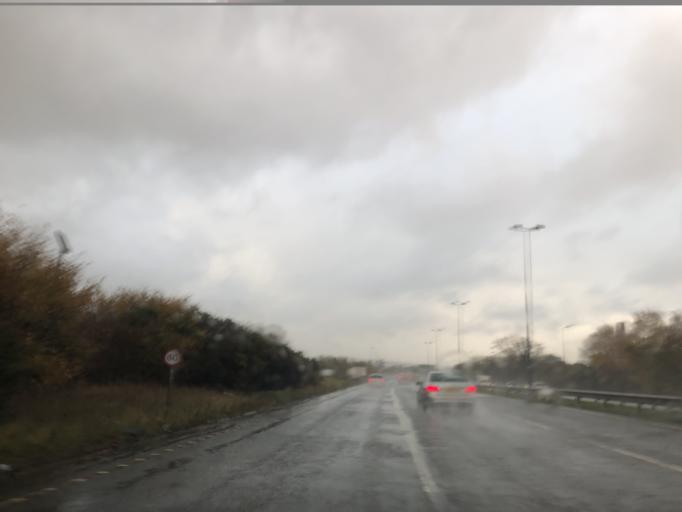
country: GB
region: England
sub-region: Solihull
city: Hampton in Arden
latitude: 52.4458
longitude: -1.7024
